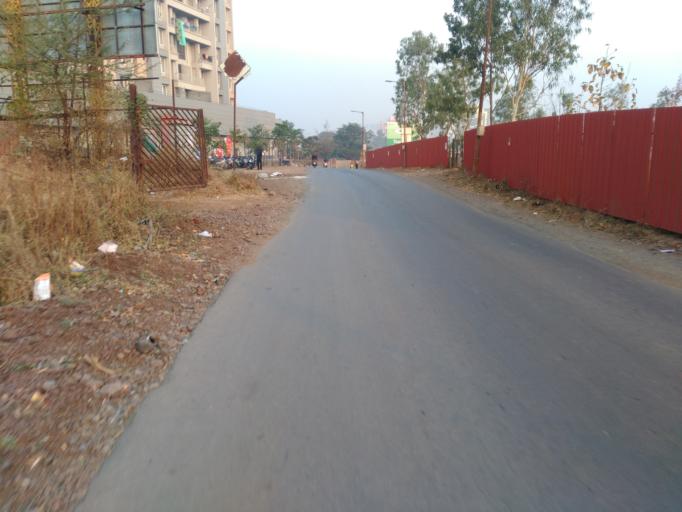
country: IN
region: Maharashtra
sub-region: Pune Division
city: Pune
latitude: 18.4493
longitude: 73.8846
